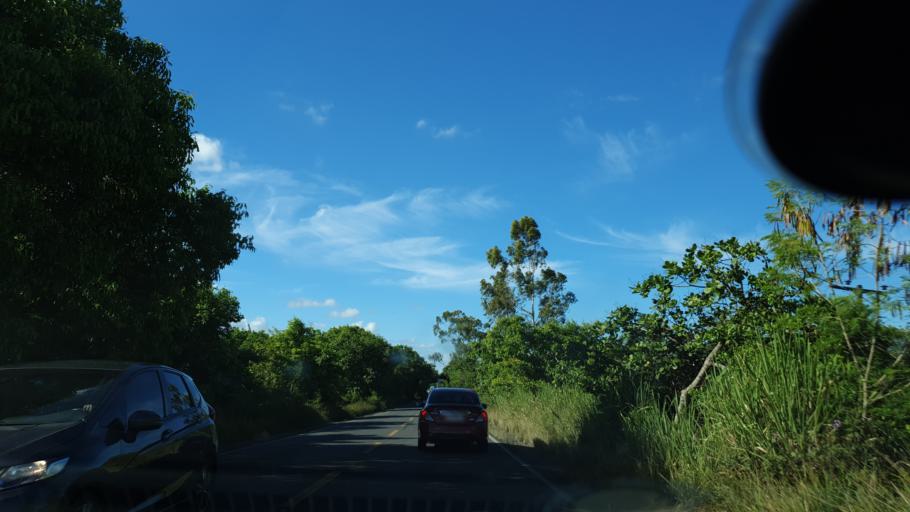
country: BR
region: Bahia
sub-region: Camacari
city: Camacari
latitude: -12.6483
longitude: -38.3039
